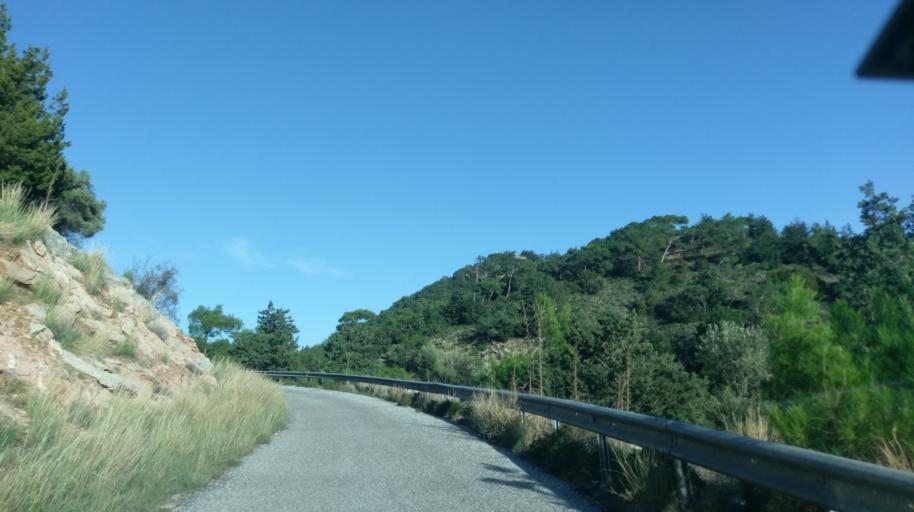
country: CY
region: Ammochostos
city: Lefkonoiko
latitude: 35.3227
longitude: 33.6234
